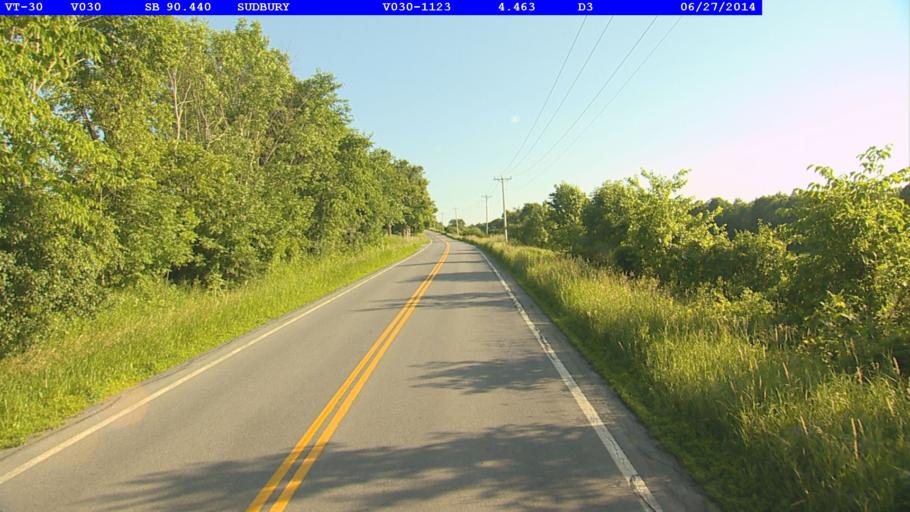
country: US
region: Vermont
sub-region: Rutland County
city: Brandon
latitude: 43.8115
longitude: -73.1993
